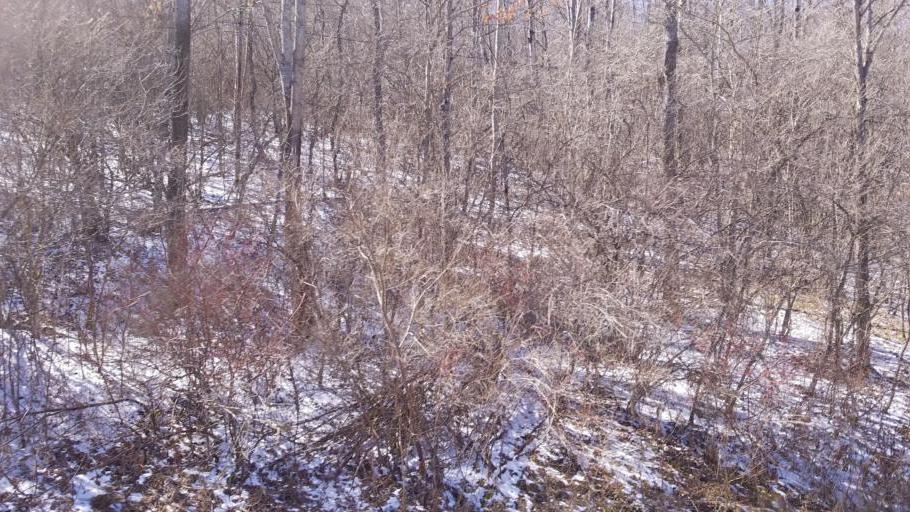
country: US
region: New York
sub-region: Allegany County
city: Wellsville
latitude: 42.0979
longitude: -77.9391
